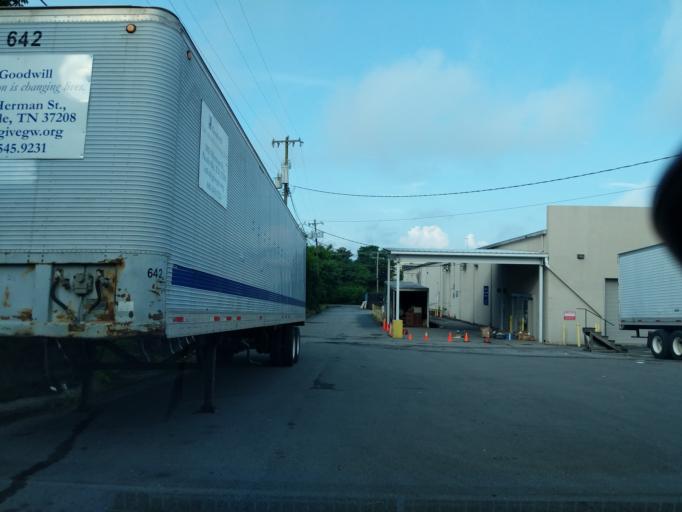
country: US
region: Tennessee
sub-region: Davidson County
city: Goodlettsville
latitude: 36.3018
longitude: -86.6898
